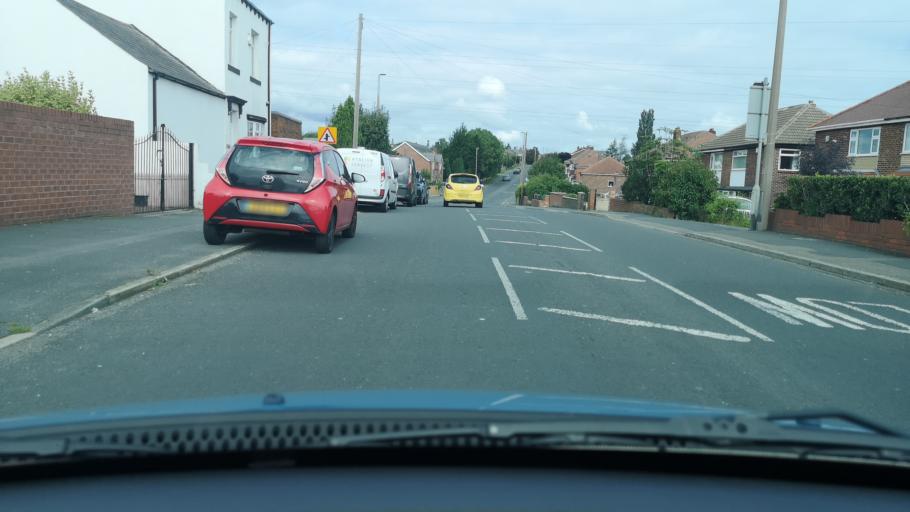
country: GB
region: England
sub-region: Kirklees
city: Liversedge
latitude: 53.6917
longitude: -1.6978
